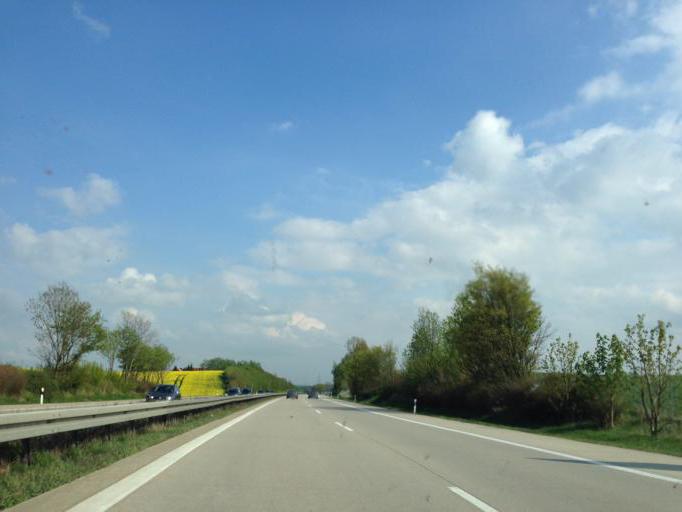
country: DE
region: Saxony
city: Grossweitzschen
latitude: 51.1650
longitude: 13.0932
